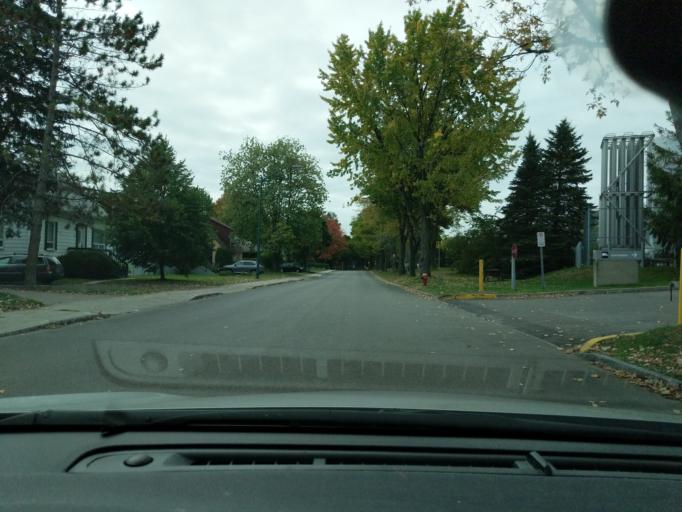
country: CA
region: Quebec
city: L'Ancienne-Lorette
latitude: 46.7676
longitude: -71.2812
